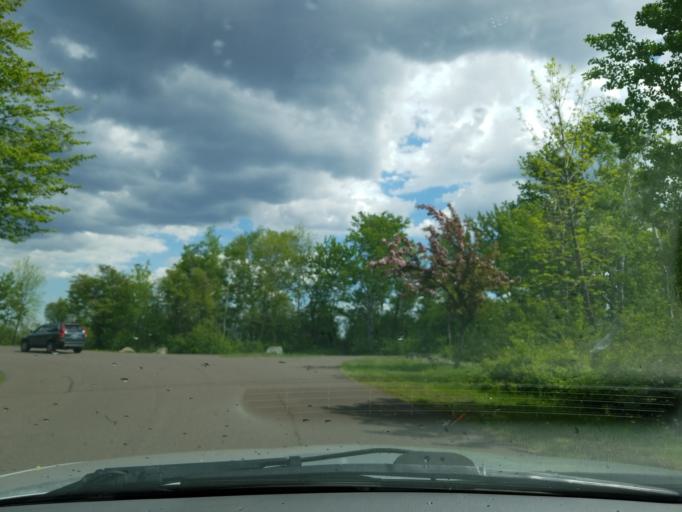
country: US
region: Minnesota
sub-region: Saint Louis County
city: Duluth
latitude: 46.7750
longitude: -92.1261
